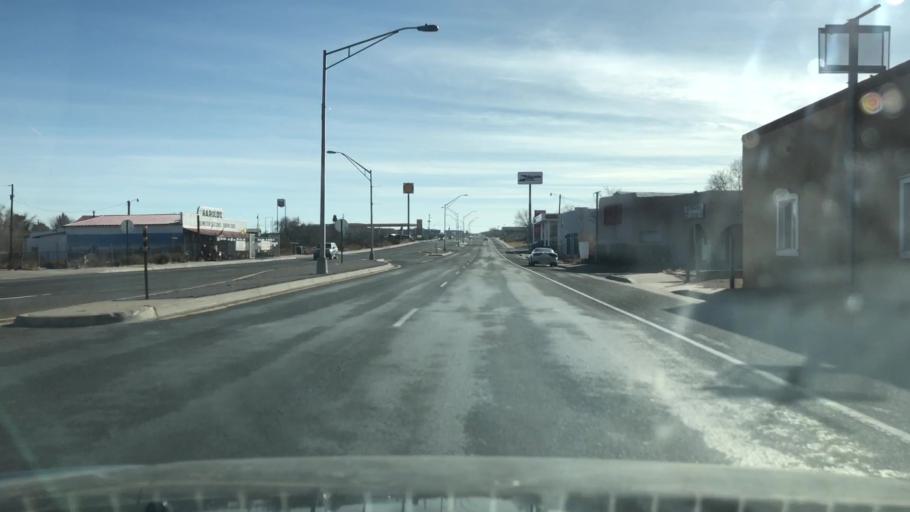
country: US
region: New Mexico
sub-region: Socorro County
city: Socorro
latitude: 34.0504
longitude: -106.8918
